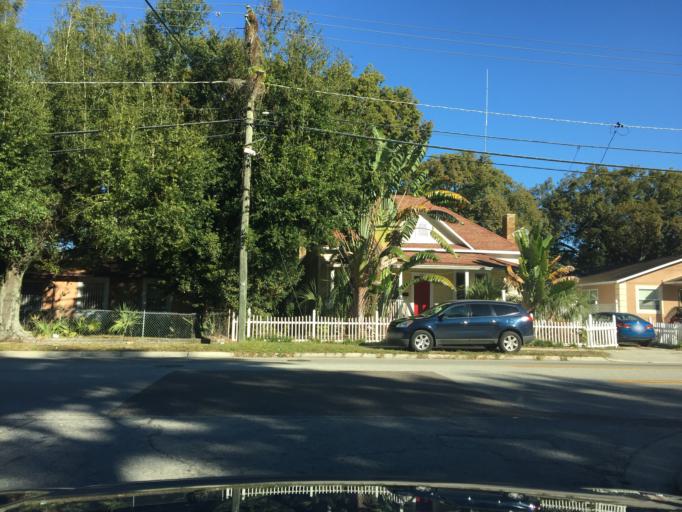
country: US
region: Florida
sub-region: Hillsborough County
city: Tampa
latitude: 27.9704
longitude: -82.4486
